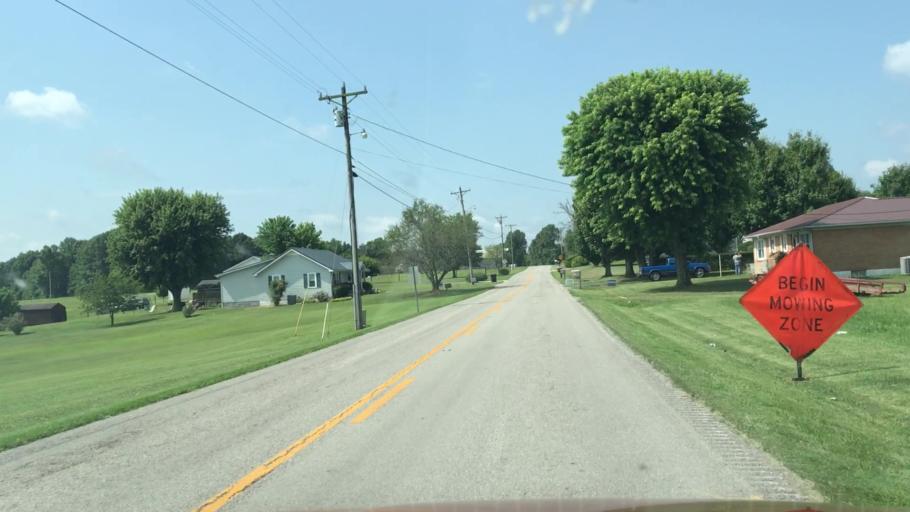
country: US
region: Kentucky
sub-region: Barren County
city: Glasgow
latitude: 36.8840
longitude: -85.8453
